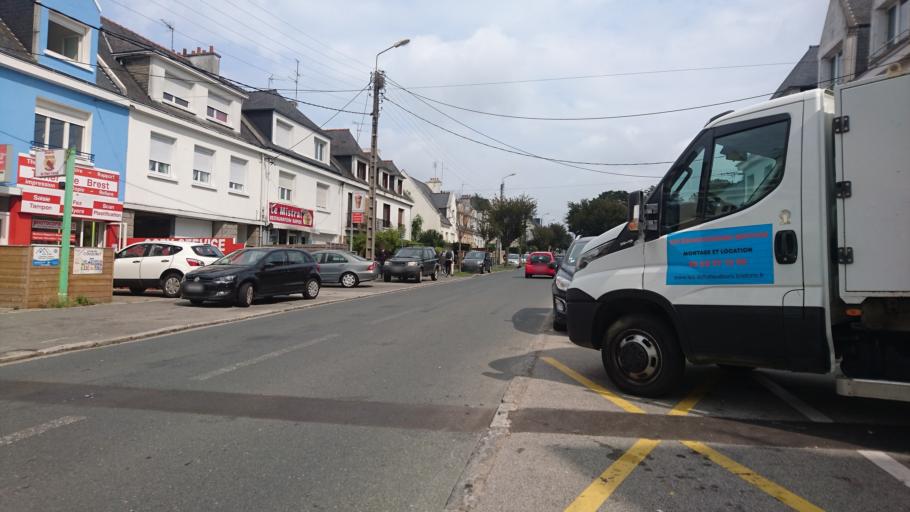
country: FR
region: Brittany
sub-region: Departement du Finistere
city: Brest
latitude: 48.4011
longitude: -4.4994
